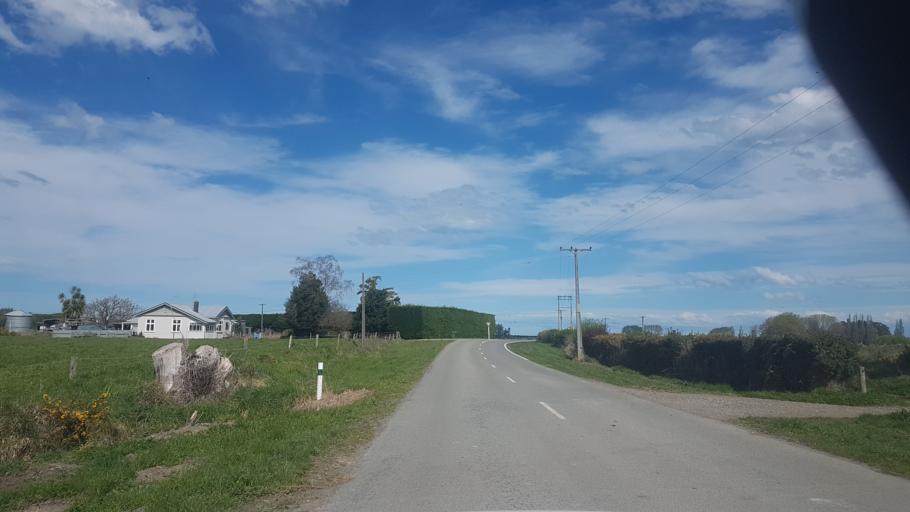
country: NZ
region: Canterbury
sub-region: Timaru District
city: Timaru
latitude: -44.2218
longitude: 171.3546
